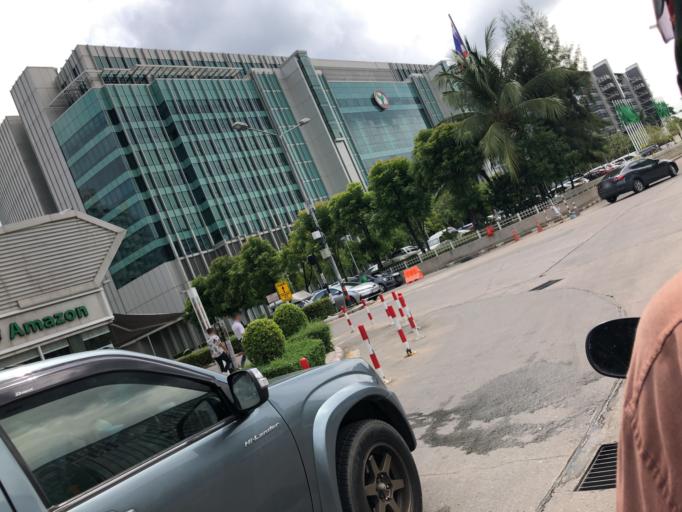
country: TH
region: Bangkok
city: Lak Si
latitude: 13.9094
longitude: 100.5521
